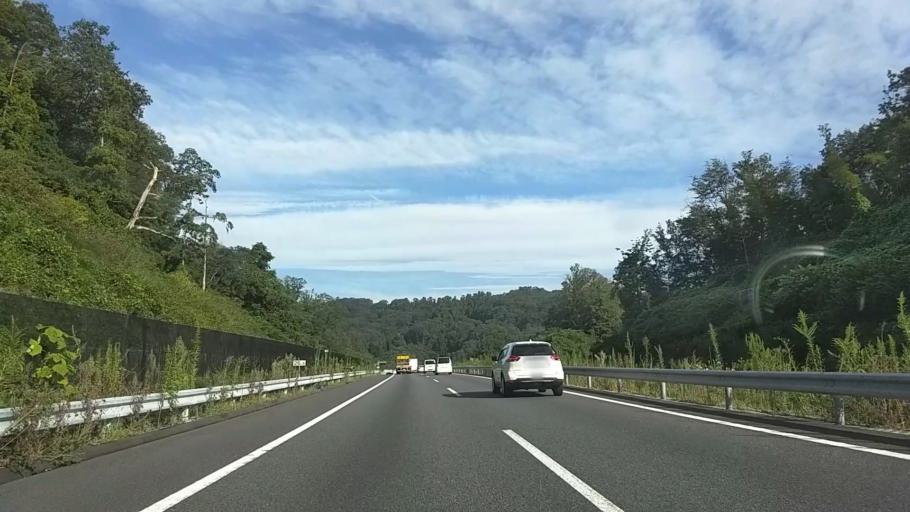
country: JP
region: Kanagawa
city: Zama
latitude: 35.5548
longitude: 139.3157
